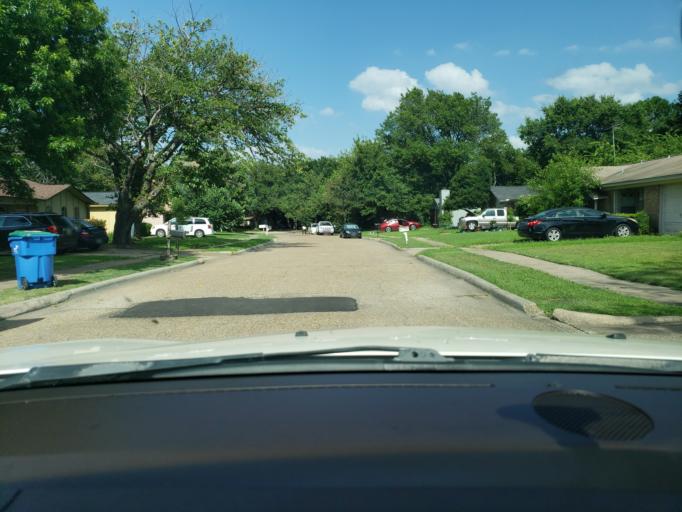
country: US
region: Texas
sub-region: Dallas County
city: Rowlett
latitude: 32.8953
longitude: -96.5727
